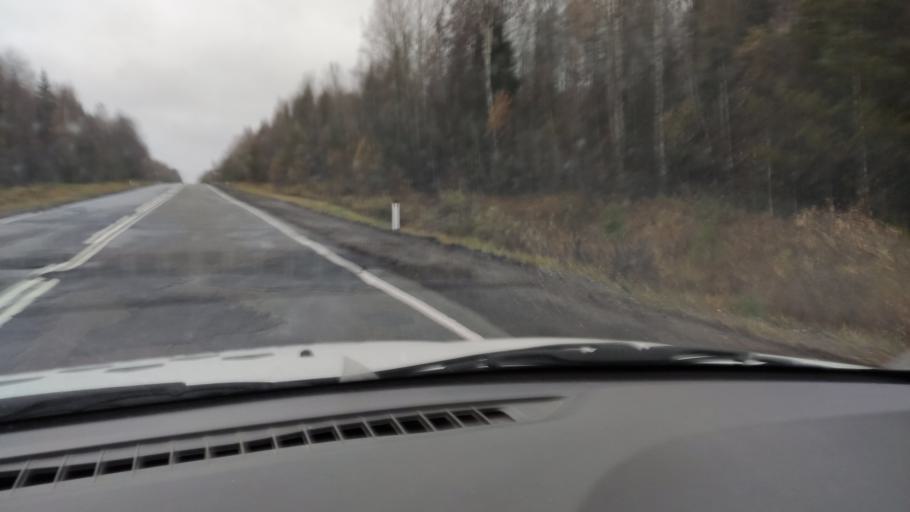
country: RU
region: Kirov
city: Omutninsk
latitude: 58.7575
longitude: 52.0273
